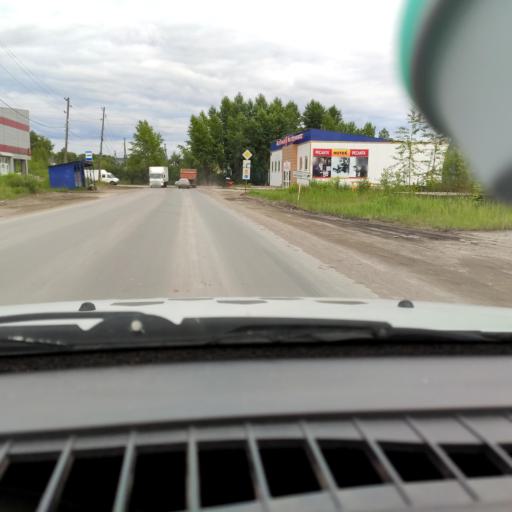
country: RU
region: Perm
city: Chusovoy
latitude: 58.2997
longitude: 57.8135
